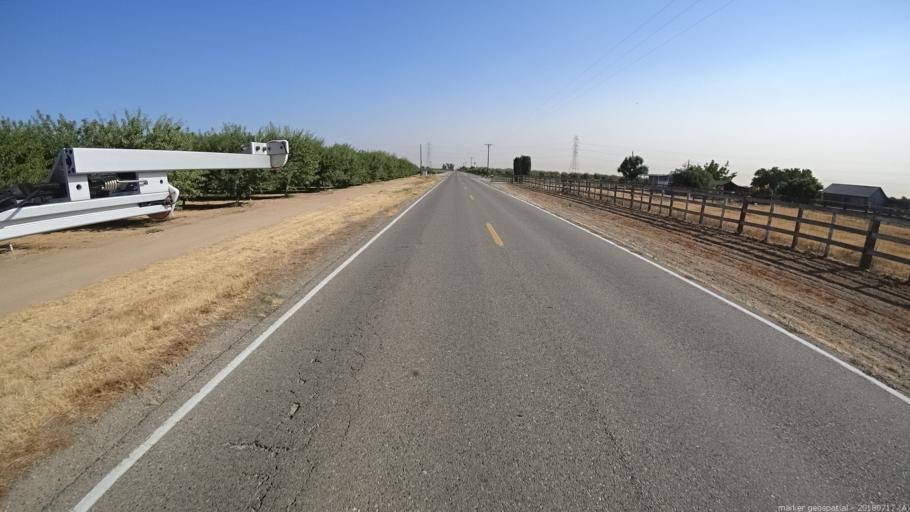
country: US
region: California
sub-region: Madera County
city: Madera Acres
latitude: 37.0391
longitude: -120.1107
